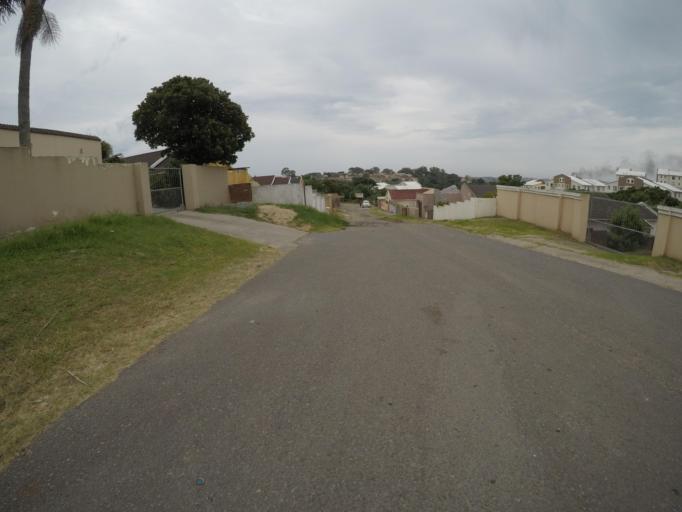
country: ZA
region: Eastern Cape
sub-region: Buffalo City Metropolitan Municipality
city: East London
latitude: -32.9938
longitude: 27.8623
